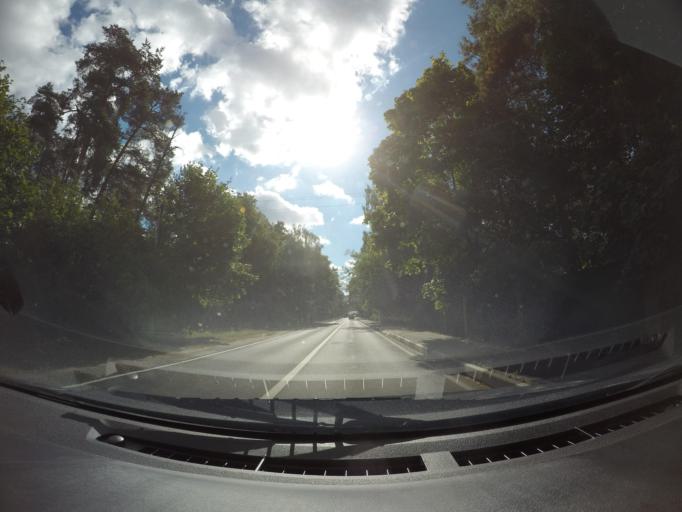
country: RU
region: Moskovskaya
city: Il'inskiy
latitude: 55.6190
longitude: 38.1187
